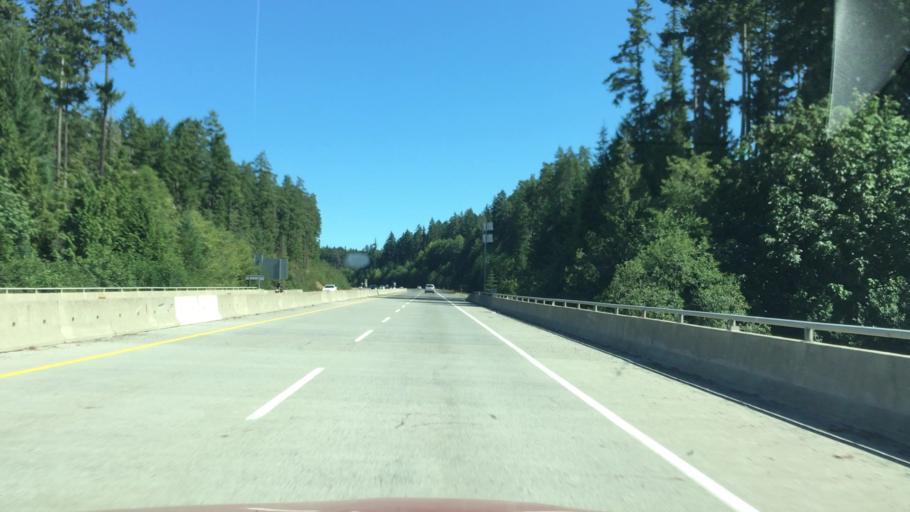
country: CA
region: British Columbia
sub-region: Regional District of Nanaimo
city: Parksville
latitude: 49.3227
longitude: -124.4122
